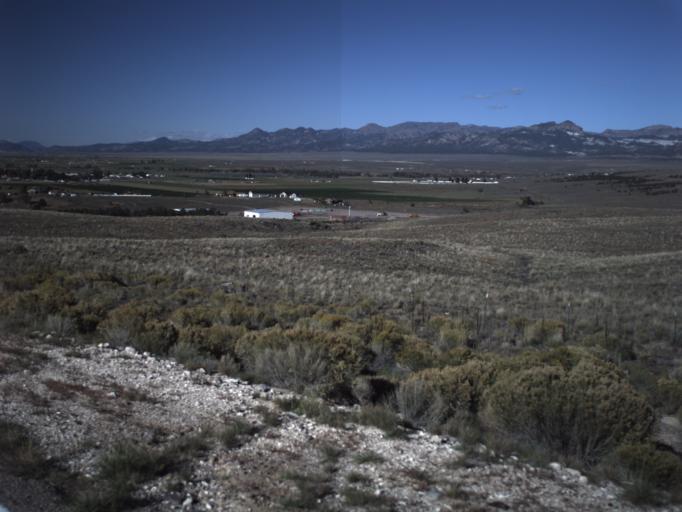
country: US
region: Utah
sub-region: Garfield County
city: Panguitch
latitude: 37.7966
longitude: -112.4372
